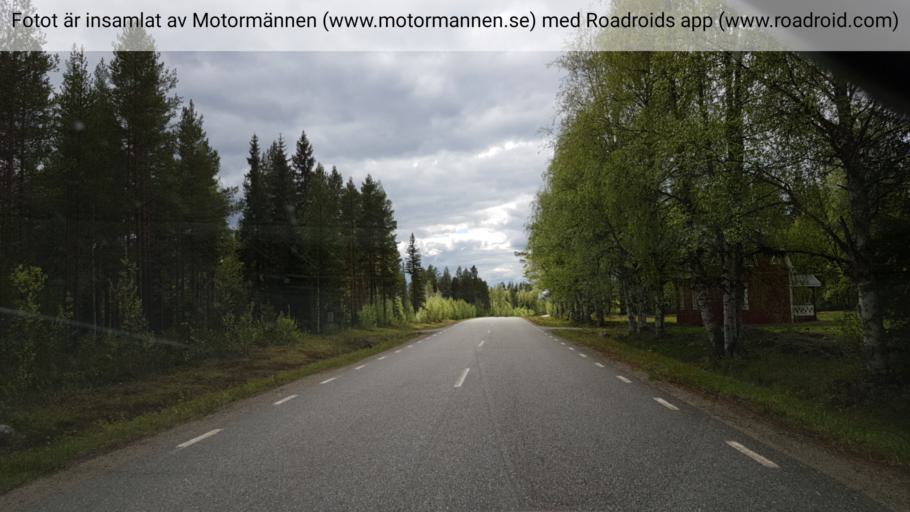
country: SE
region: Vaesterbotten
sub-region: Skelleftea Kommun
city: Langsele
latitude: 64.6187
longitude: 19.9727
